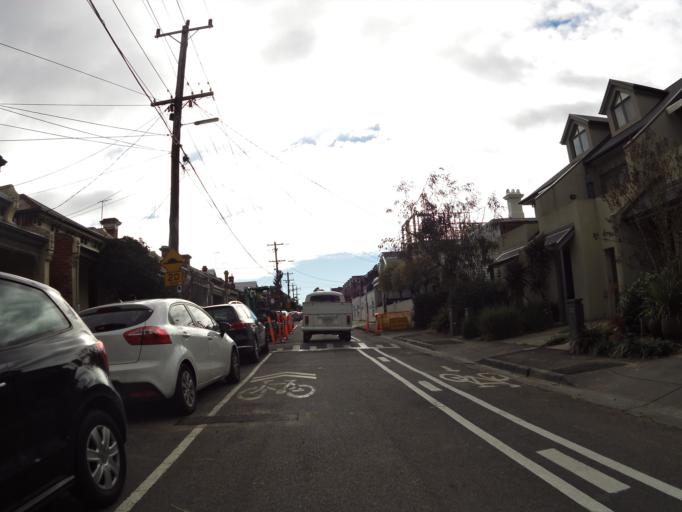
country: AU
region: Victoria
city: Abbotsford
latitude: -37.7927
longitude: 145.0009
